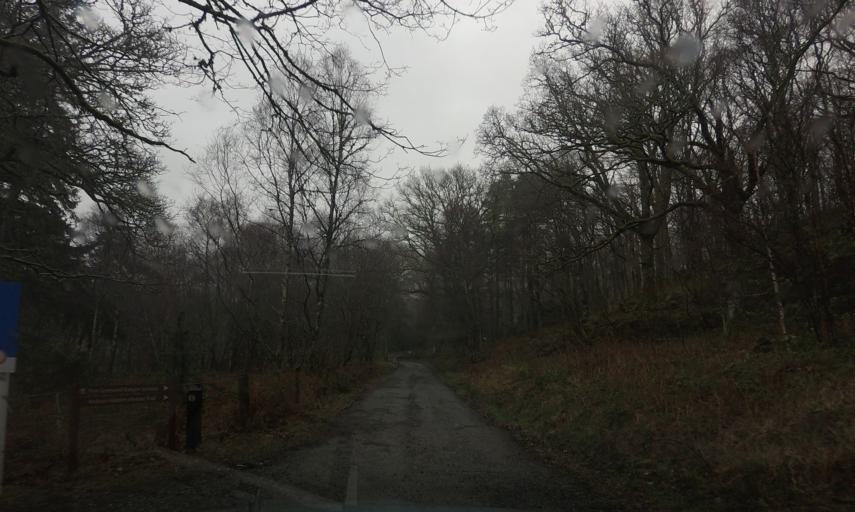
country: GB
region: Scotland
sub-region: West Dunbartonshire
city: Balloch
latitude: 56.1562
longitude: -4.6422
